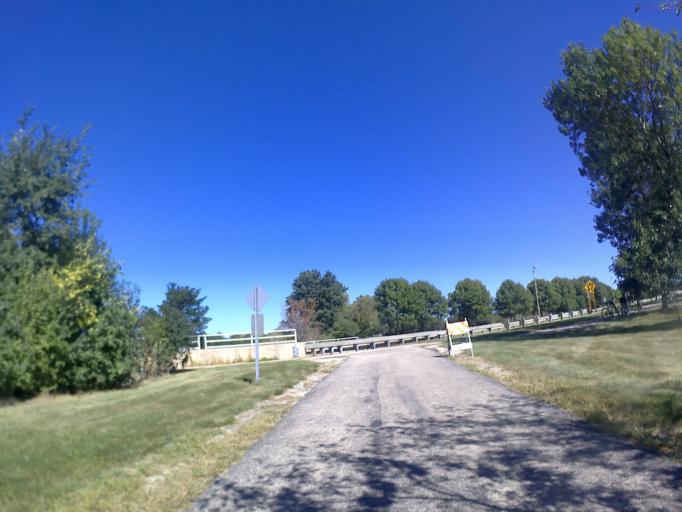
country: US
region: Illinois
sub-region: DuPage County
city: Warrenville
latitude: 41.8070
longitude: -88.1747
